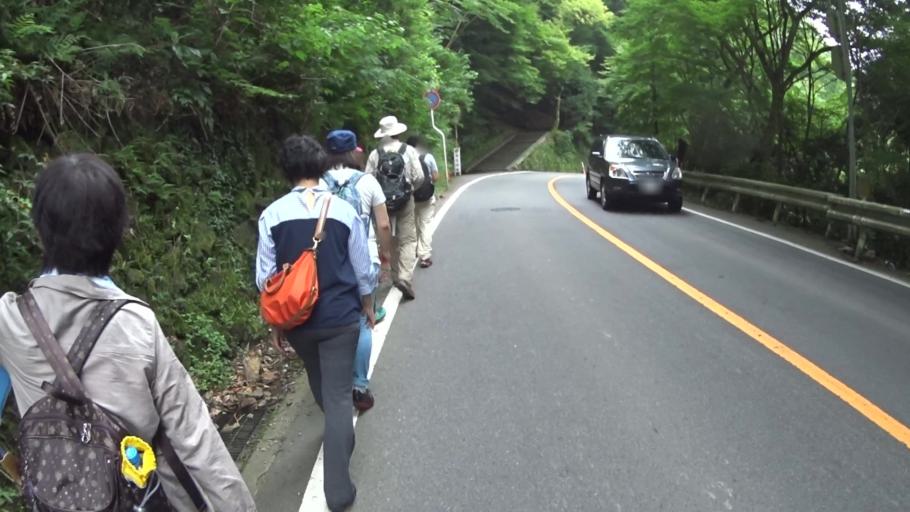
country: JP
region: Kyoto
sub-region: Kyoto-shi
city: Kamigyo-ku
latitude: 35.0588
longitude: 135.6778
